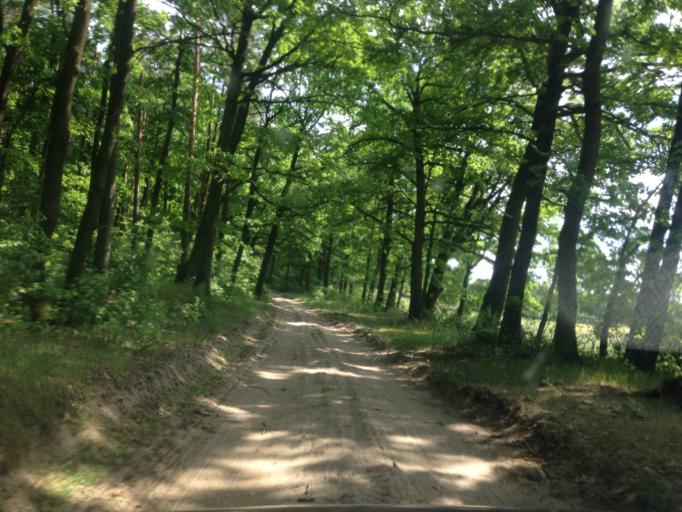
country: PL
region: Kujawsko-Pomorskie
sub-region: Powiat brodnicki
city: Gorzno
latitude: 53.1783
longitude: 19.6497
